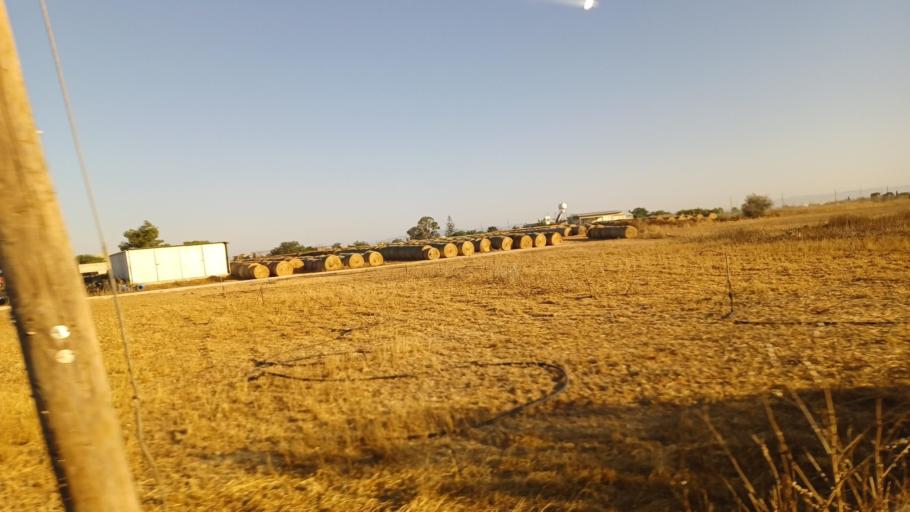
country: CY
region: Ammochostos
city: Avgorou
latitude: 35.0066
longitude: 33.8358
